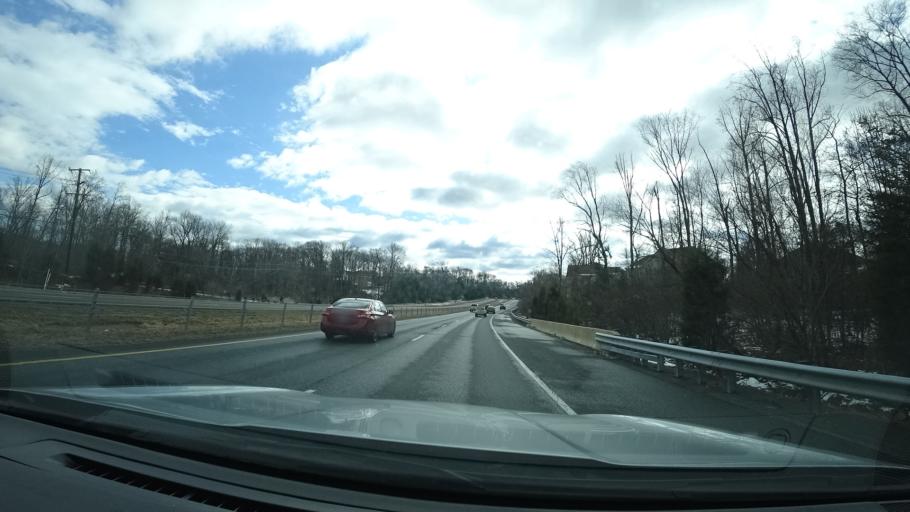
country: US
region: Virginia
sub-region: Fairfax County
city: Dranesville
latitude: 38.9882
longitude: -77.3604
